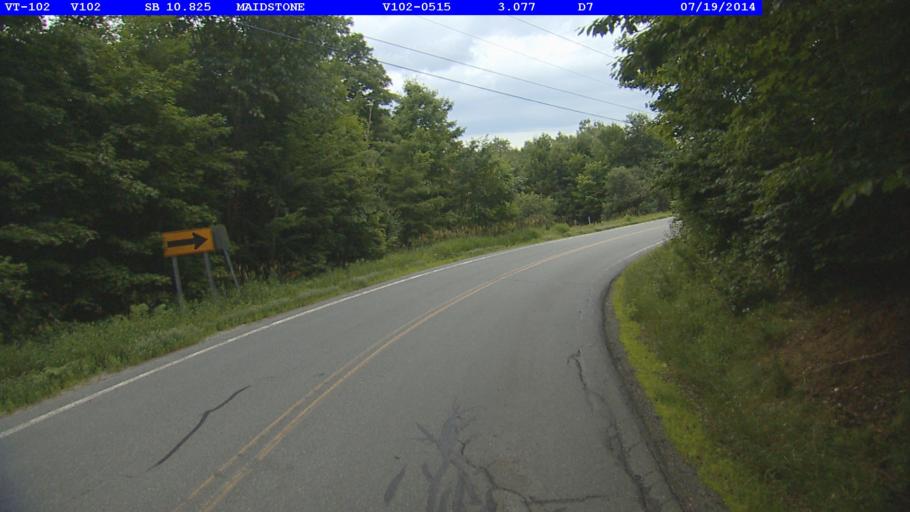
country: US
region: Vermont
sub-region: Essex County
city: Guildhall
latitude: 44.6069
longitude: -71.5601
